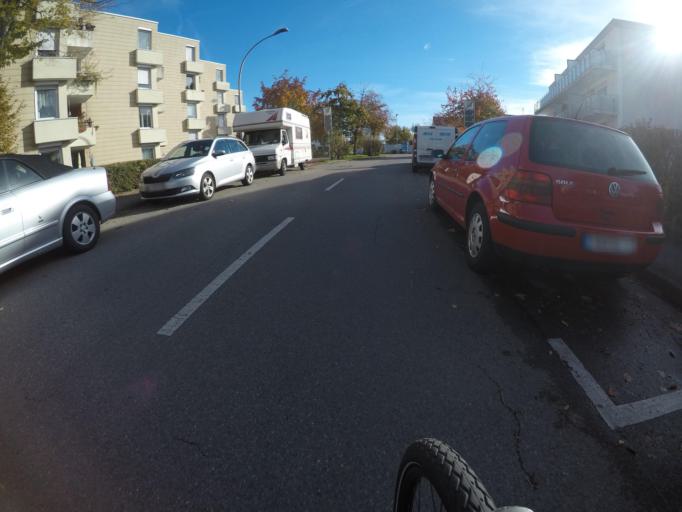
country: DE
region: Baden-Wuerttemberg
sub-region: Regierungsbezirk Stuttgart
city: Leinfelden-Echterdingen
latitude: 48.6835
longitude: 9.1591
